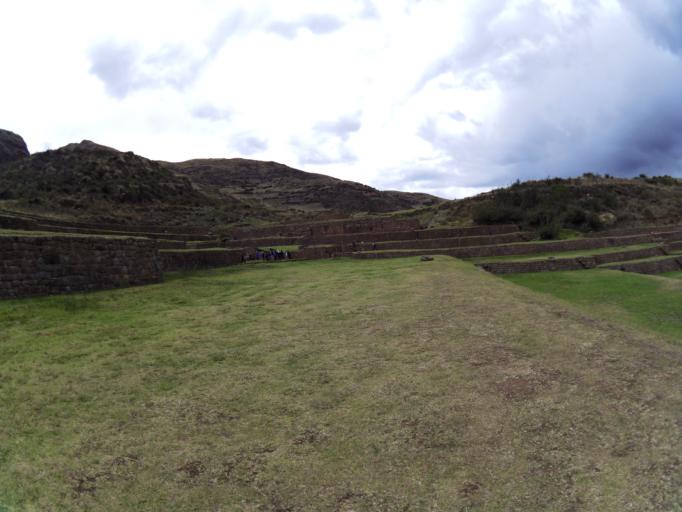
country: PE
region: Cusco
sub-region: Provincia de Quispicanchis
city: Oropesa
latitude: -13.5694
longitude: -71.7824
